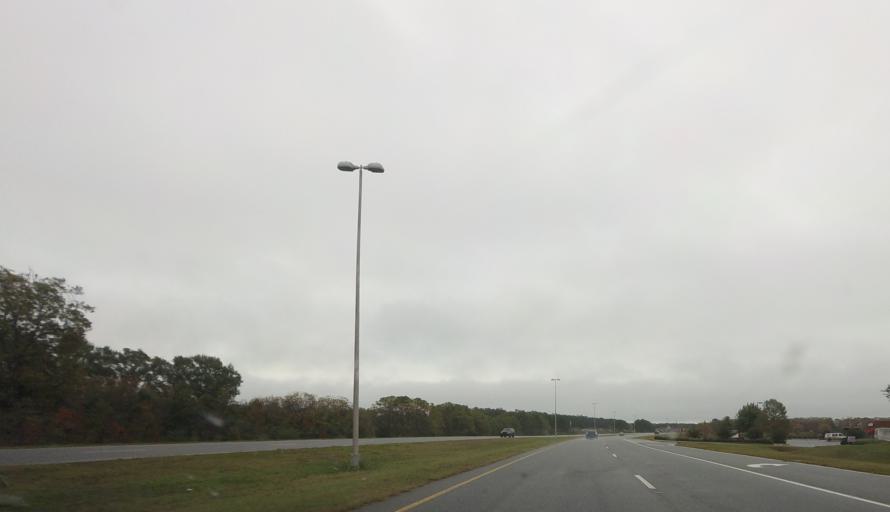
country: US
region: Georgia
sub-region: Houston County
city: Centerville
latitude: 32.5807
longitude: -83.7086
